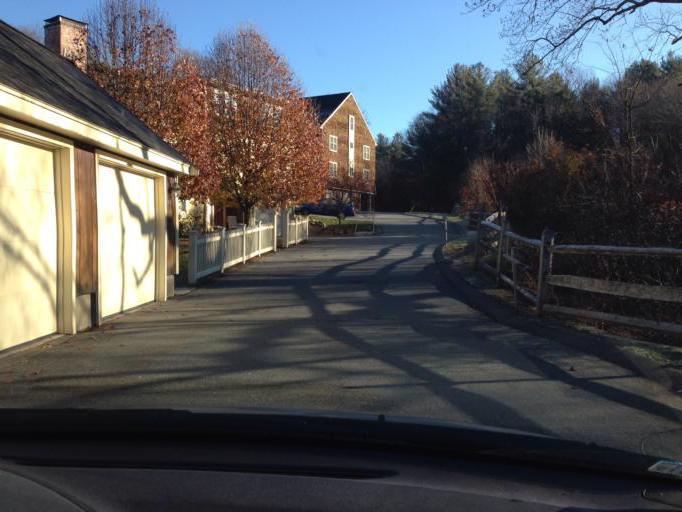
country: US
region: Massachusetts
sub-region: Middlesex County
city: Bedford
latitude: 42.5182
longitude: -71.2849
